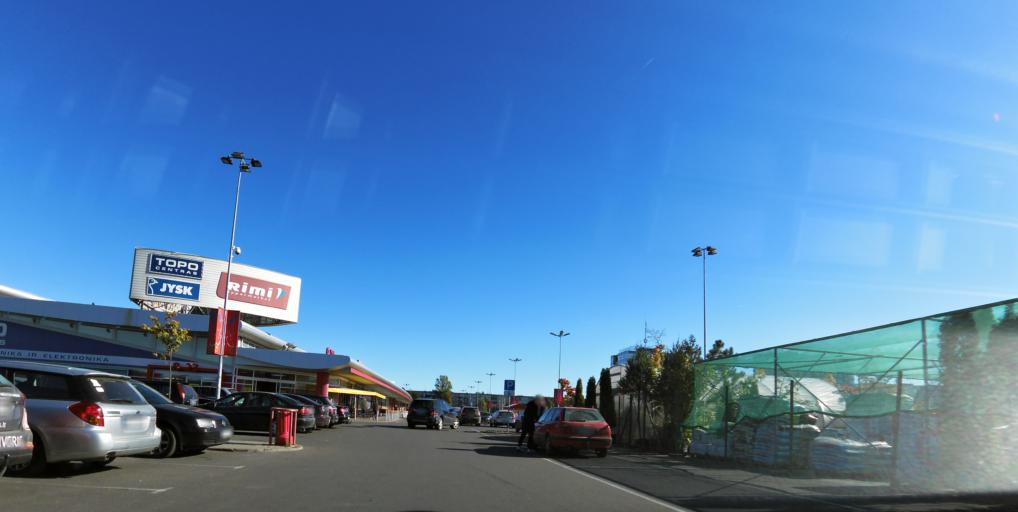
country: LT
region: Vilnius County
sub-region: Vilnius
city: Vilnius
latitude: 54.7118
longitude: 25.3000
